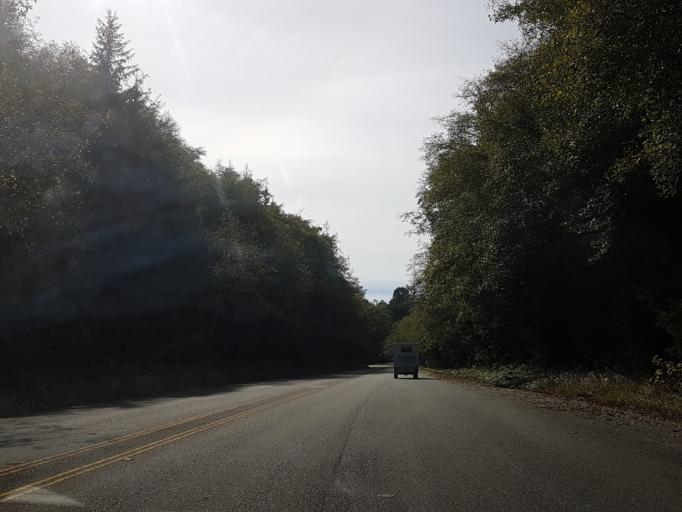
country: US
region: California
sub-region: Del Norte County
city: Bertsch-Oceanview
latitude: 41.4640
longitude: -124.0430
